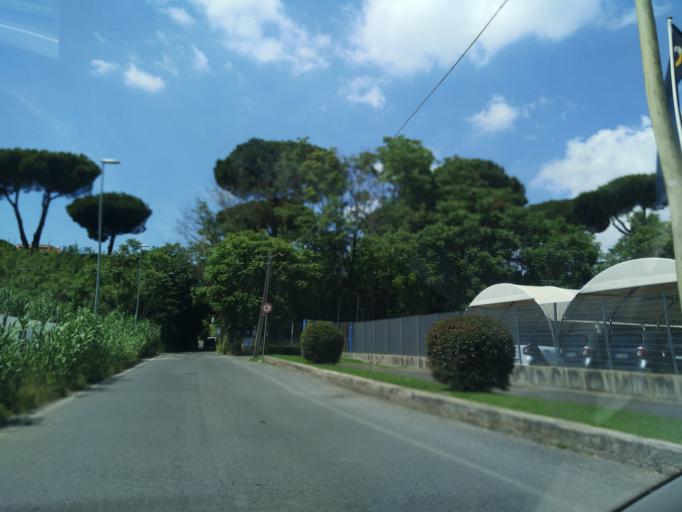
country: IT
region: Latium
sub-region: Citta metropolitana di Roma Capitale
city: Selcetta
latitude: 41.8079
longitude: 12.4550
